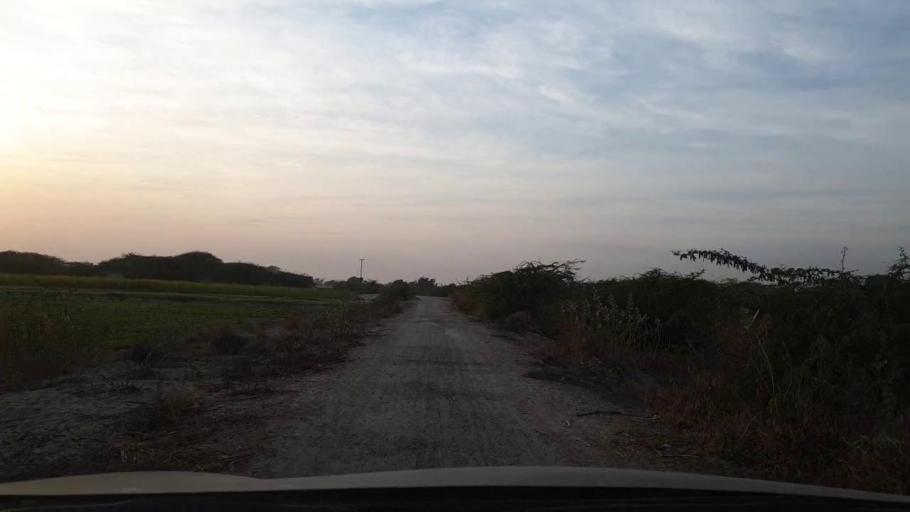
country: PK
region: Sindh
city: Tando Adam
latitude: 25.6766
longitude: 68.7090
